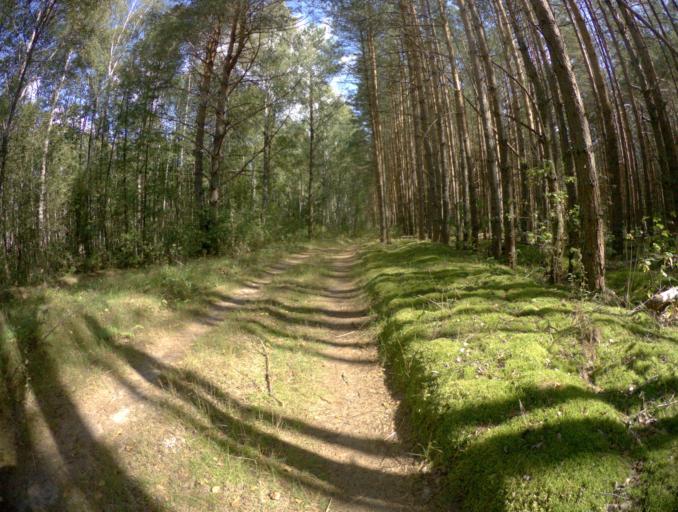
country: RU
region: Vladimir
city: Pokrov
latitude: 55.8518
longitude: 39.2684
